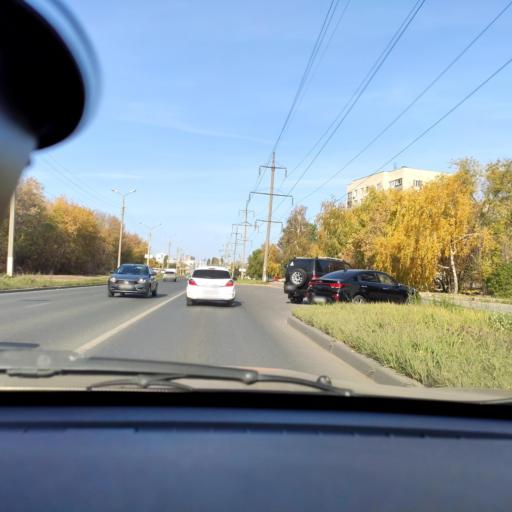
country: RU
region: Samara
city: Tol'yatti
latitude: 53.5260
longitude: 49.3963
